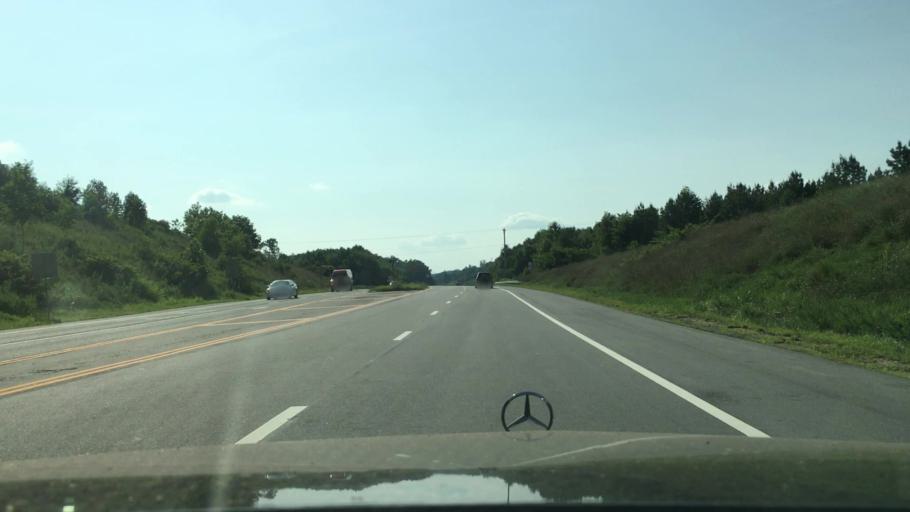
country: US
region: Virginia
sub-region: Amherst County
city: Madison Heights
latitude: 37.4087
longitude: -79.0866
